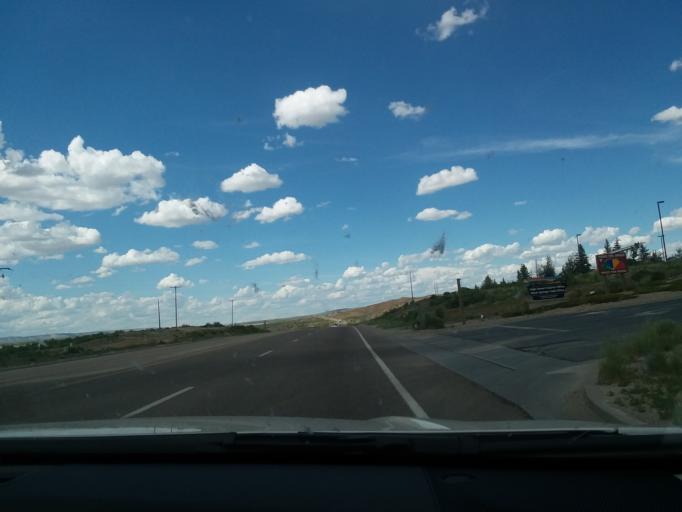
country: US
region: Wyoming
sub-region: Sweetwater County
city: North Rock Springs
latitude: 41.6276
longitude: -109.2324
